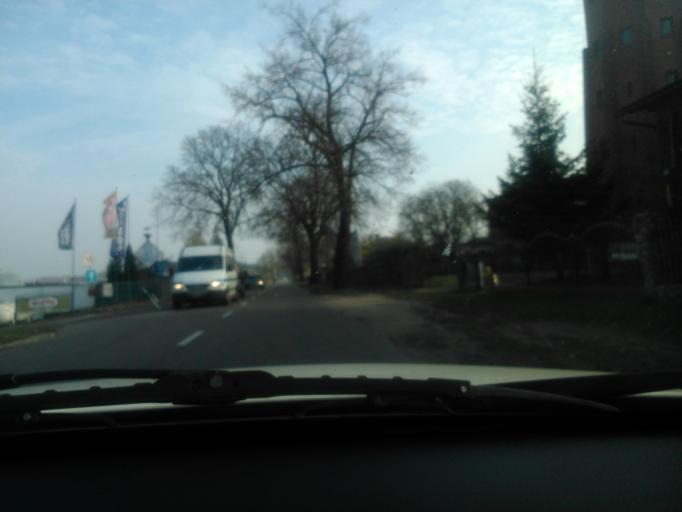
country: PL
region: Warmian-Masurian Voivodeship
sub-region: Powiat dzialdowski
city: Lidzbark
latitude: 53.2625
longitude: 19.8427
